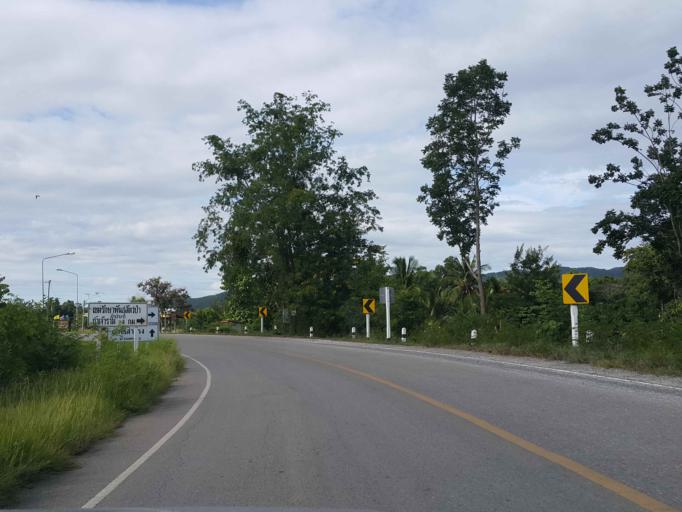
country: TH
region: Sukhothai
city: Thung Saliam
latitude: 17.2317
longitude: 99.5120
